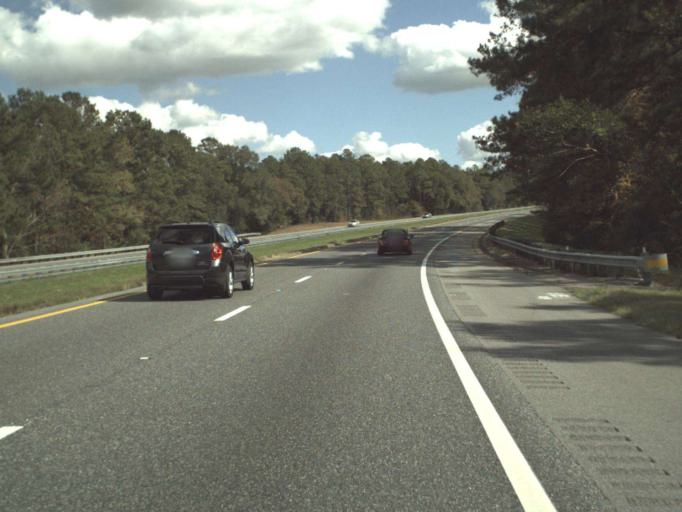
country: US
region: Florida
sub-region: Gadsden County
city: Gretna
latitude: 30.6099
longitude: -84.7458
